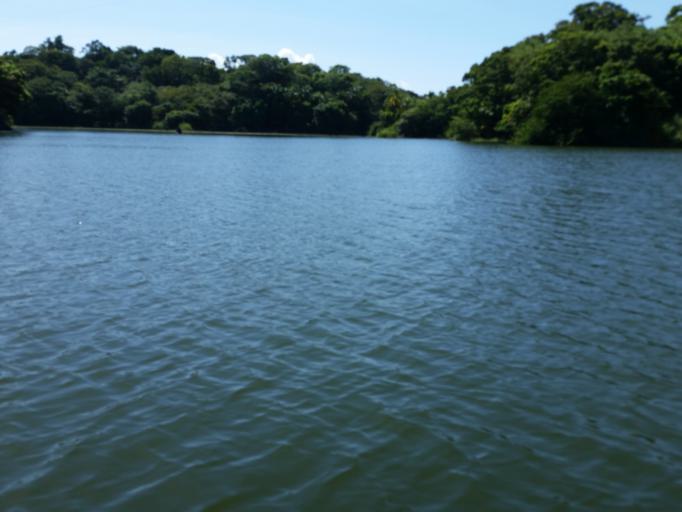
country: NI
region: Granada
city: Granada
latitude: 11.8784
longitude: -85.8985
